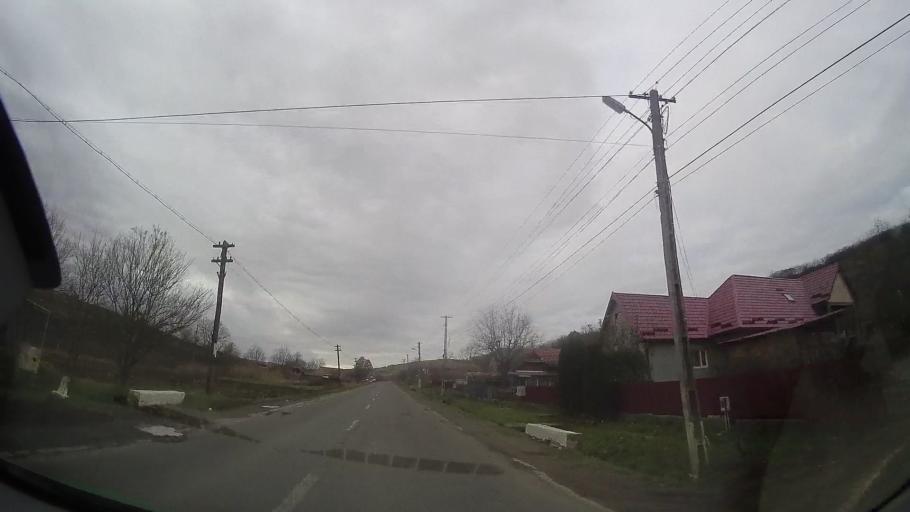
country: RO
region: Mures
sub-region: Comuna Craesti
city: Craiesti
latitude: 46.7573
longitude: 24.4128
